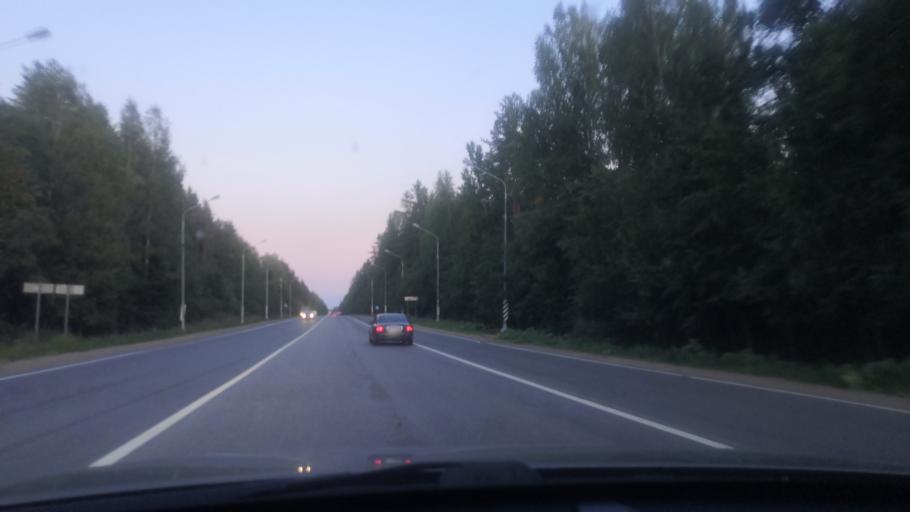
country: RU
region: St.-Petersburg
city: Pesochnyy
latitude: 60.1878
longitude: 30.1042
